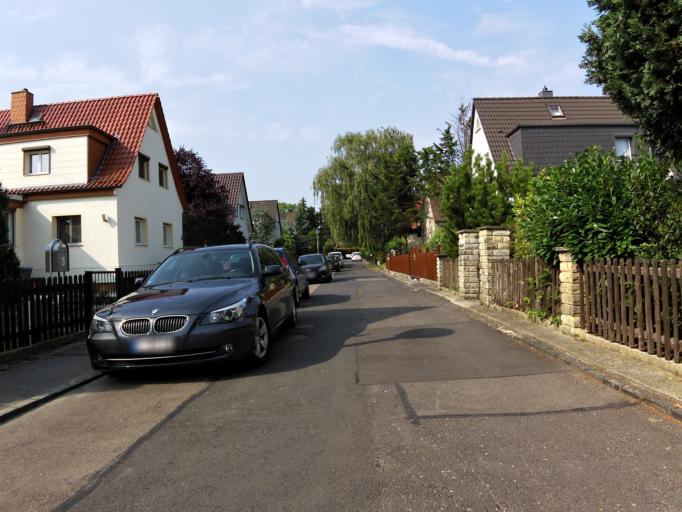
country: DE
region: Saxony
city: Leipzig
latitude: 51.3831
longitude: 12.3851
